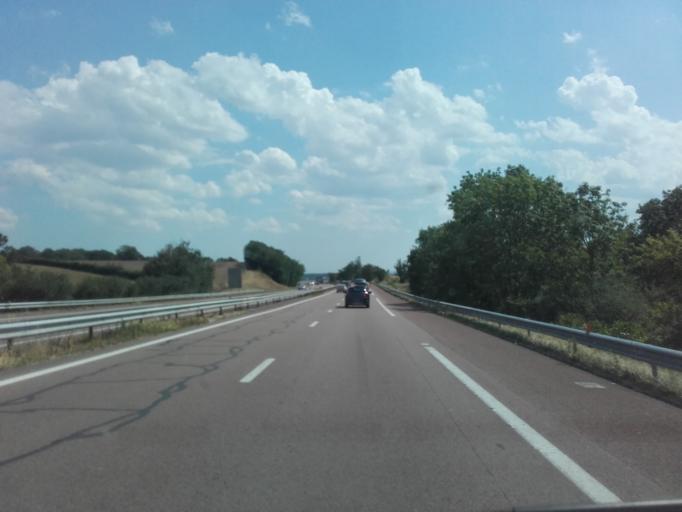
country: FR
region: Bourgogne
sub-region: Departement de l'Yonne
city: Avallon
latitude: 47.5567
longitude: 3.9506
